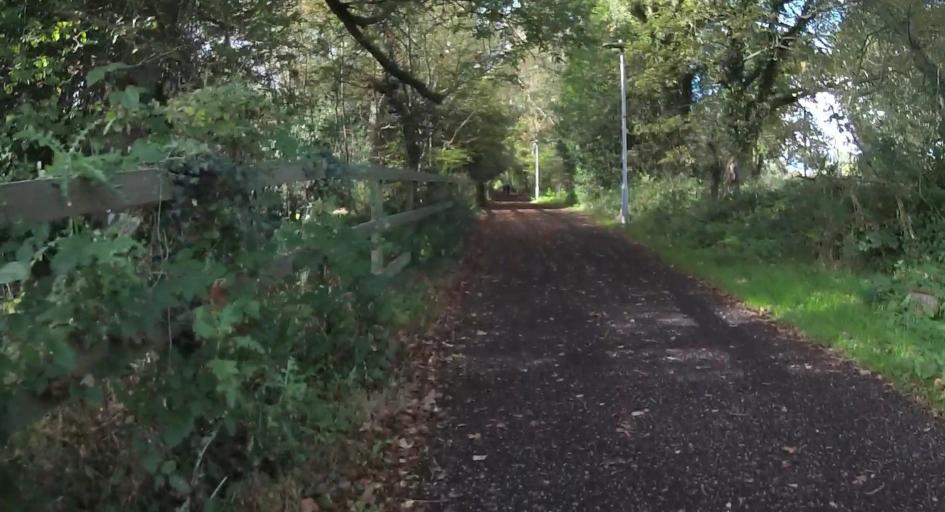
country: GB
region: England
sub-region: Wokingham
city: Barkham
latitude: 51.3834
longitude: -0.8794
